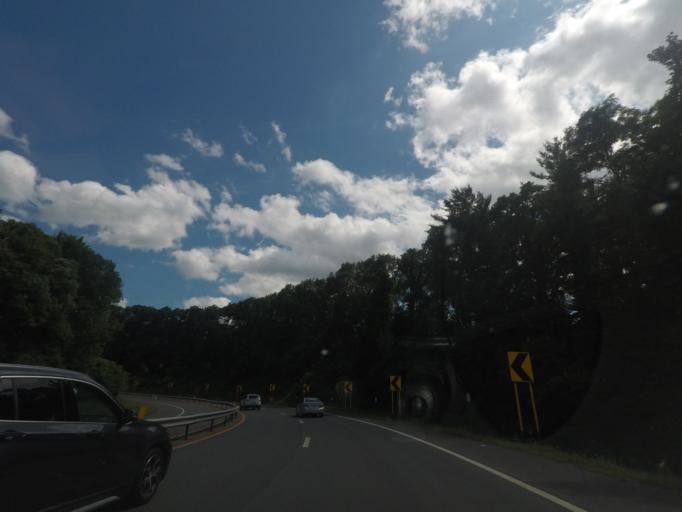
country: US
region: New York
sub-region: Schenectady County
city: Rotterdam
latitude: 42.7525
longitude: -73.9347
